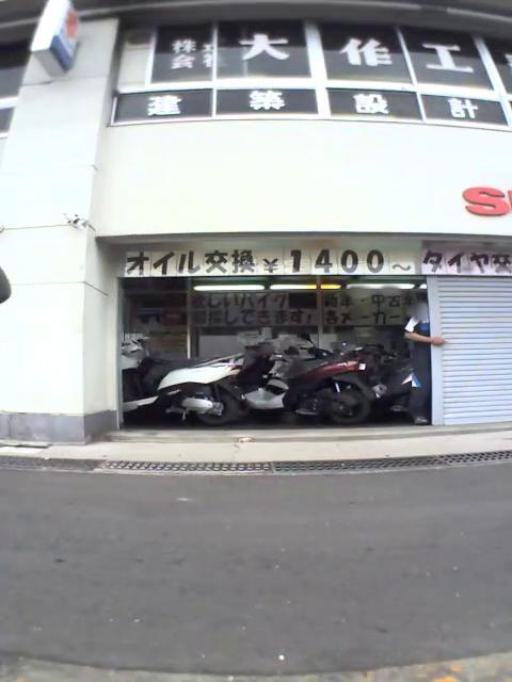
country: JP
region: Osaka
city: Neyagawa
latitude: 34.7754
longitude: 135.6316
